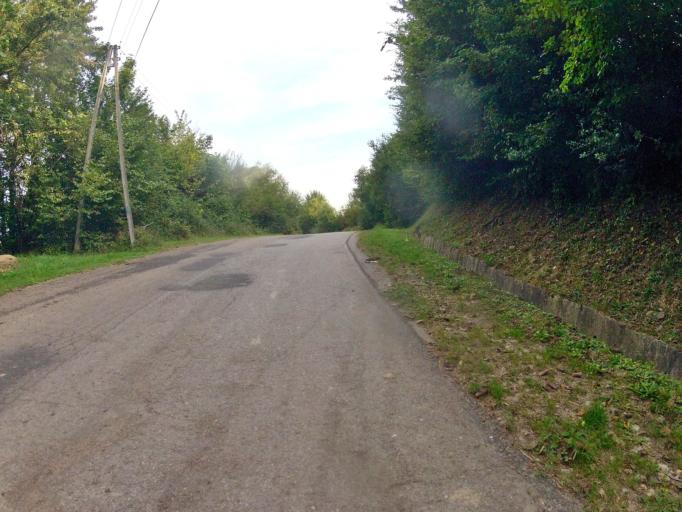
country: PL
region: Subcarpathian Voivodeship
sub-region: Powiat jasielski
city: Krempna
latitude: 49.5418
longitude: 21.5526
